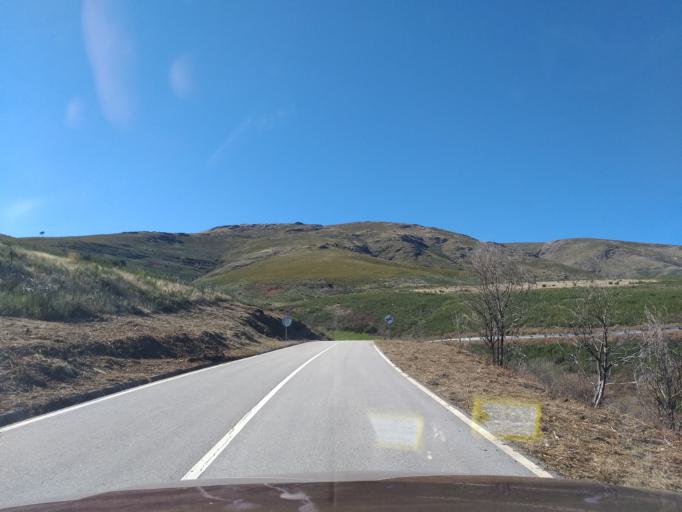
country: PT
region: Guarda
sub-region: Manteigas
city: Manteigas
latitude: 40.4608
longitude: -7.5125
